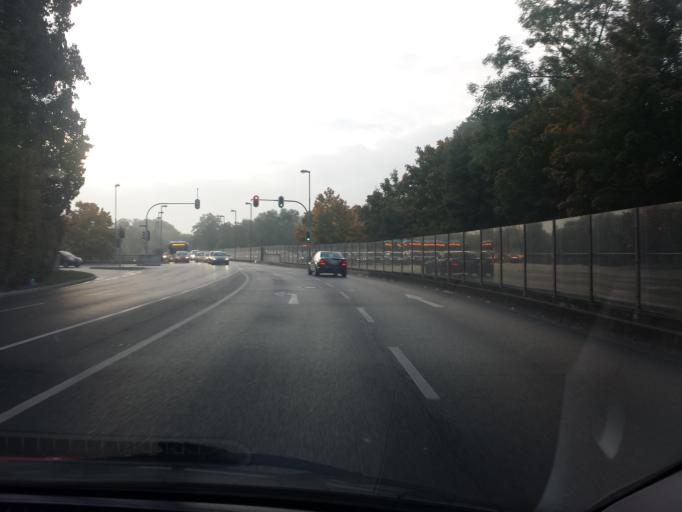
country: DE
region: Bavaria
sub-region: Upper Bavaria
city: Ingolstadt
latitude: 48.7574
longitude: 11.4224
